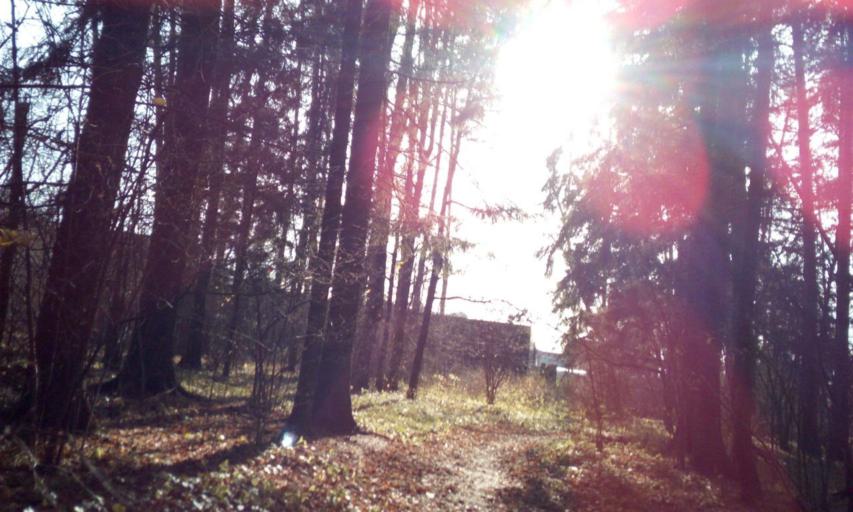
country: RU
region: Moskovskaya
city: Zhavoronki
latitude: 55.6596
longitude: 37.1537
